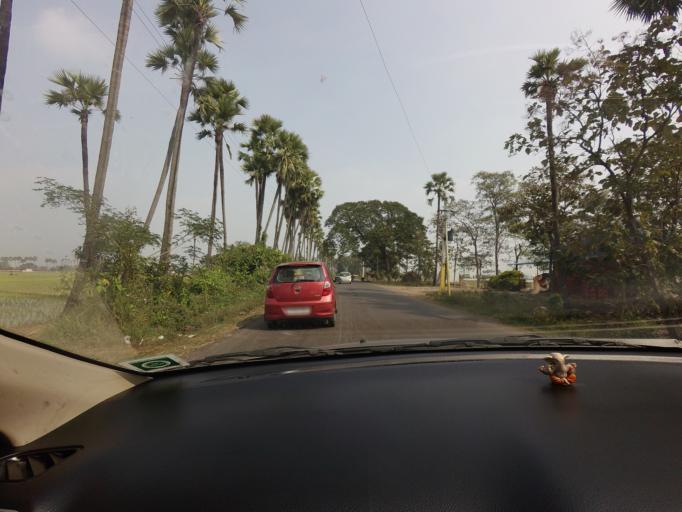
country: IN
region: Andhra Pradesh
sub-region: Krishna
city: Kankipadu
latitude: 16.4540
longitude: 80.7885
